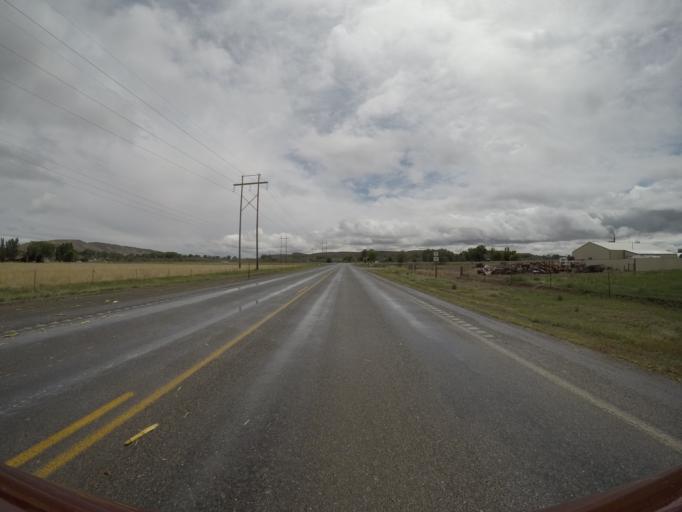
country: US
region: Wyoming
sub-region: Big Horn County
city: Lovell
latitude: 44.8426
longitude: -108.3316
